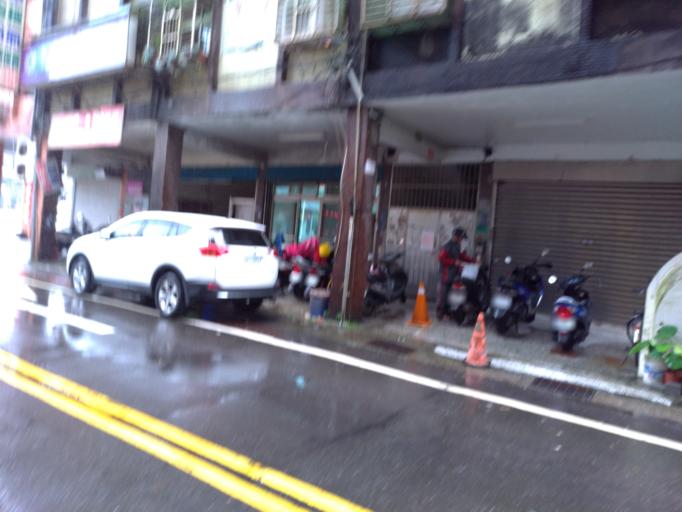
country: TW
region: Taiwan
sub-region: Keelung
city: Keelung
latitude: 25.0872
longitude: 121.6954
